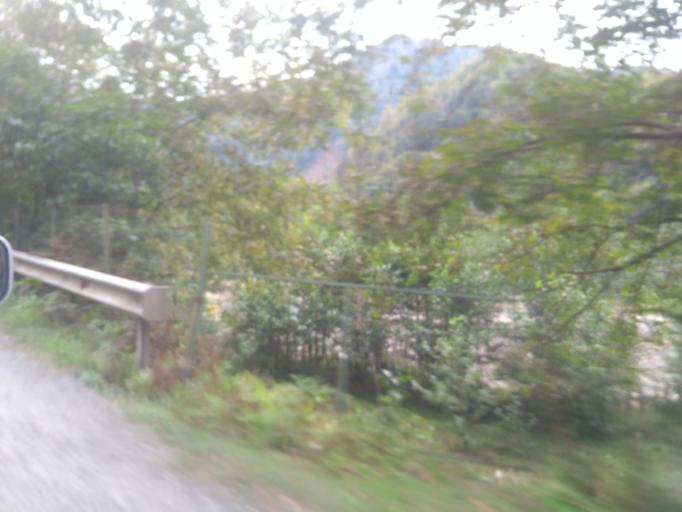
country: TR
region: Artvin
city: Muratli
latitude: 41.5452
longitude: 41.7653
